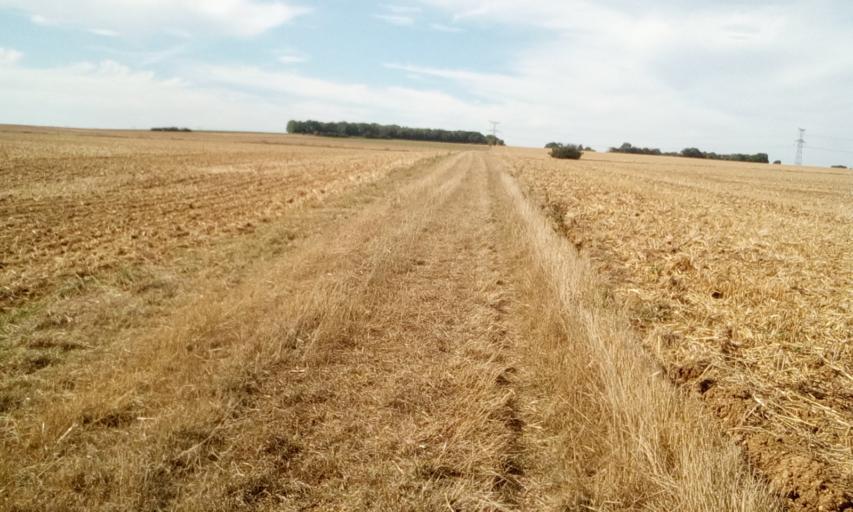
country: FR
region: Lower Normandy
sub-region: Departement du Calvados
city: Fontaine-Etoupefour
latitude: 49.1126
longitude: -0.4495
